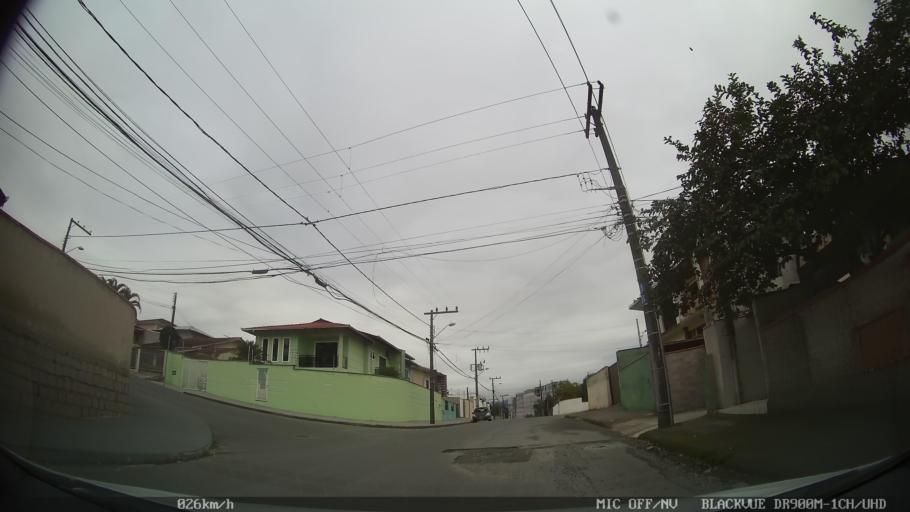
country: BR
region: Santa Catarina
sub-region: Joinville
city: Joinville
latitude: -26.2691
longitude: -48.8866
